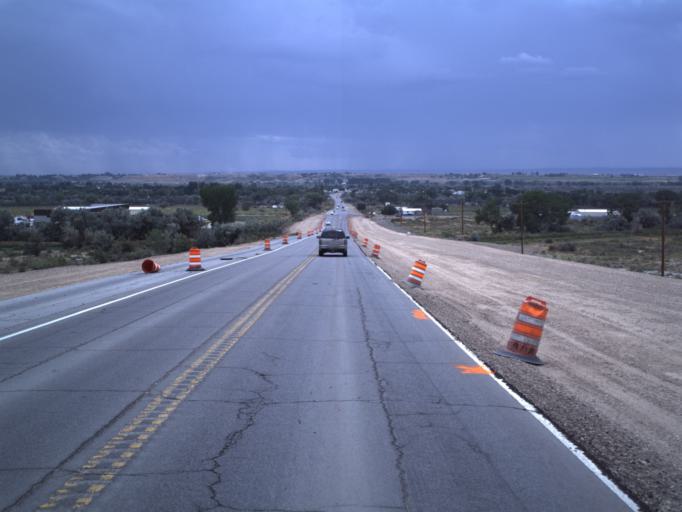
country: US
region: Utah
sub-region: Duchesne County
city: Roosevelt
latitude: 40.2170
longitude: -110.0674
